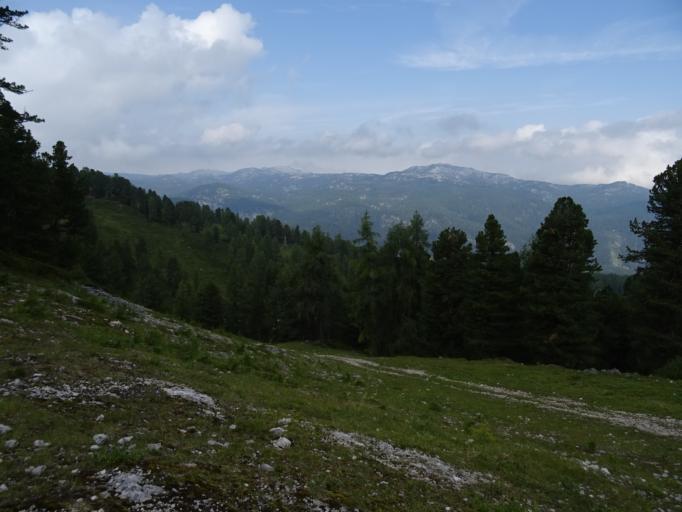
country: AT
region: Styria
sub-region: Politischer Bezirk Liezen
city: Aich
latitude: 47.4587
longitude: 13.8192
